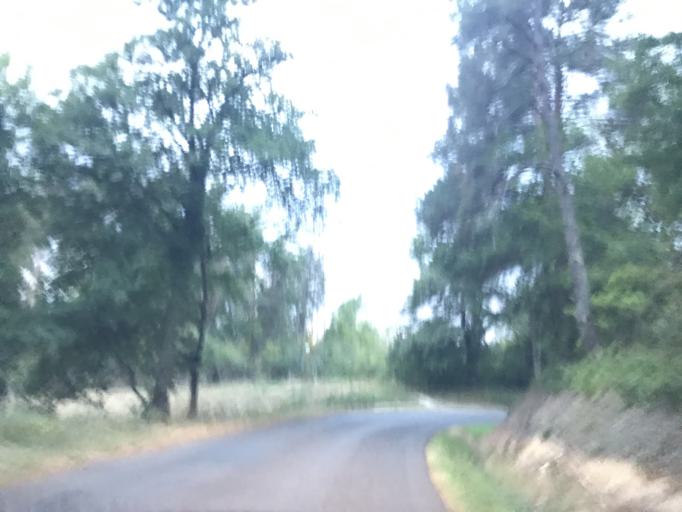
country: FR
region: Auvergne
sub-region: Departement du Puy-de-Dome
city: Escoutoux
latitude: 45.8106
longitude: 3.5628
